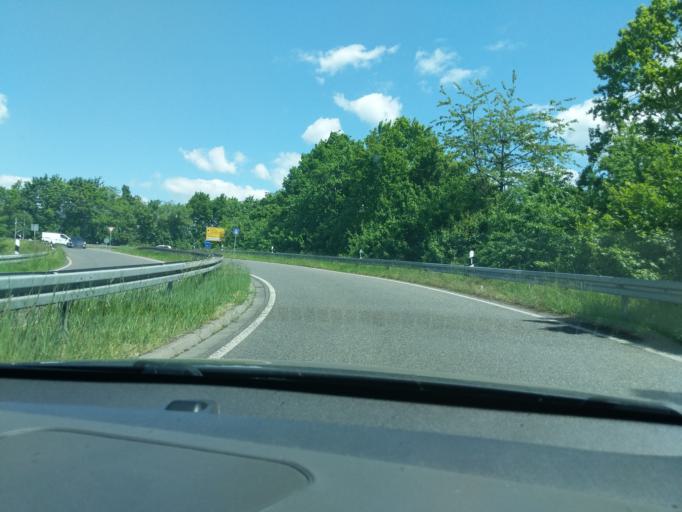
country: DE
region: Hesse
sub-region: Regierungsbezirk Darmstadt
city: Maintal
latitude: 50.1470
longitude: 8.8273
